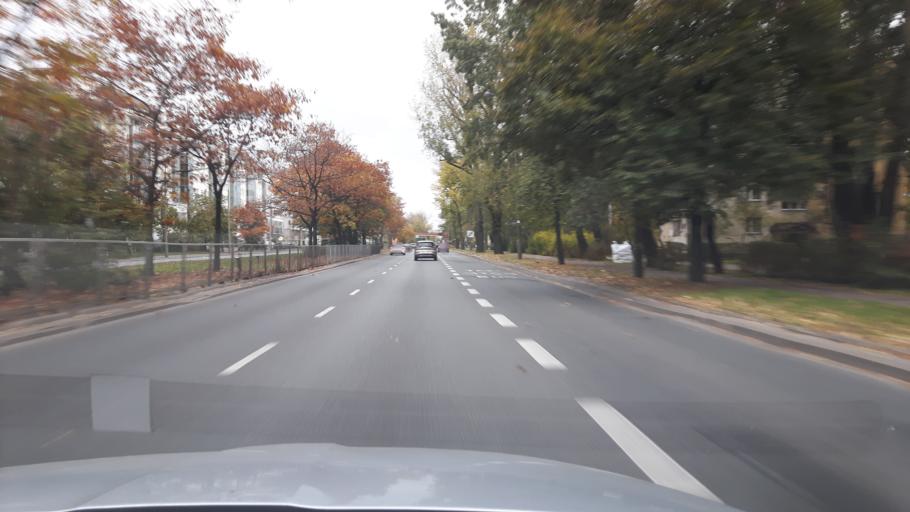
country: PL
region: Masovian Voivodeship
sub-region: Warszawa
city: Mokotow
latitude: 52.2000
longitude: 21.0369
